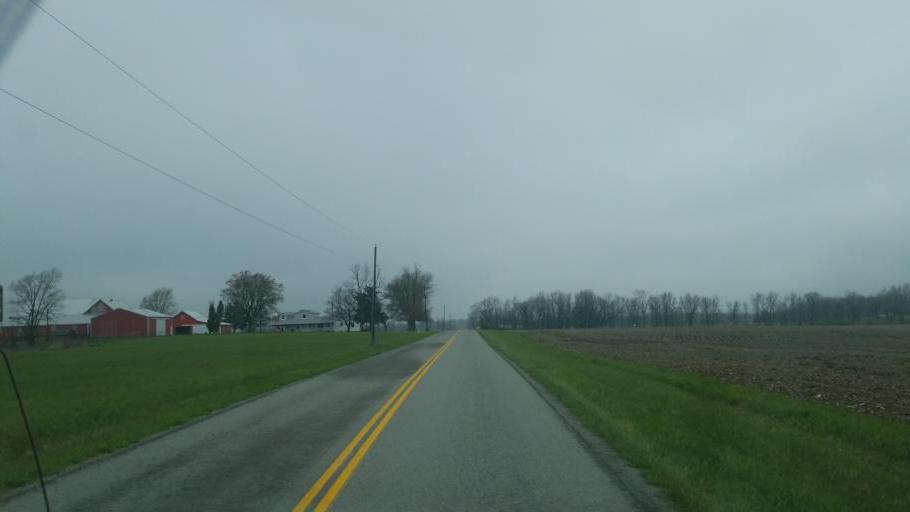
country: US
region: Ohio
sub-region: Logan County
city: Northwood
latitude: 40.4864
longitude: -83.6744
